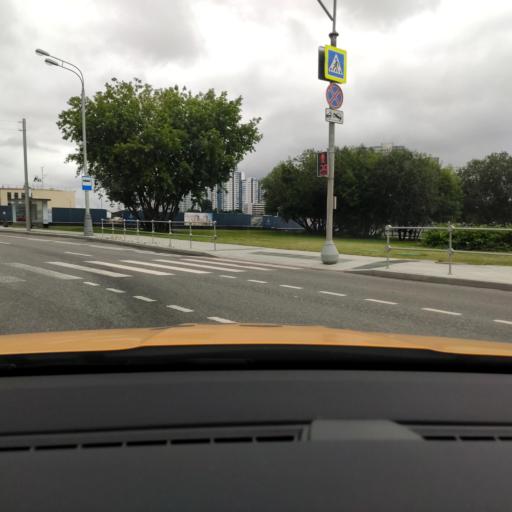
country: RU
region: Moskovskaya
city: Kozhukhovo
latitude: 55.6886
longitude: 37.6727
